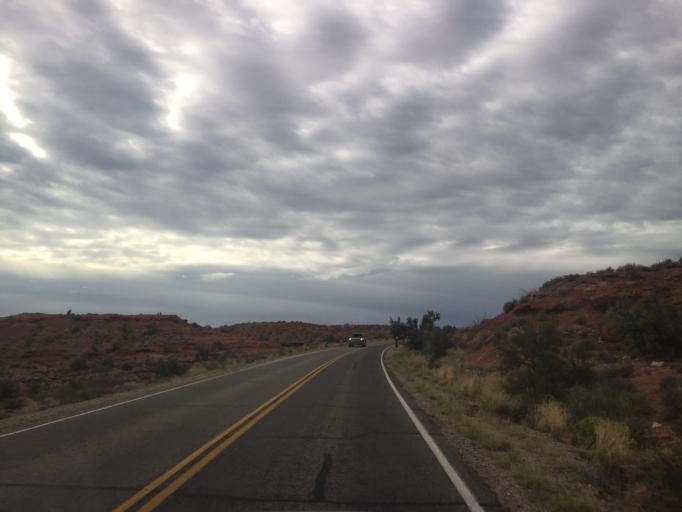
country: US
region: Utah
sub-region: Grand County
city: Moab
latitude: 38.6280
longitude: -109.5932
